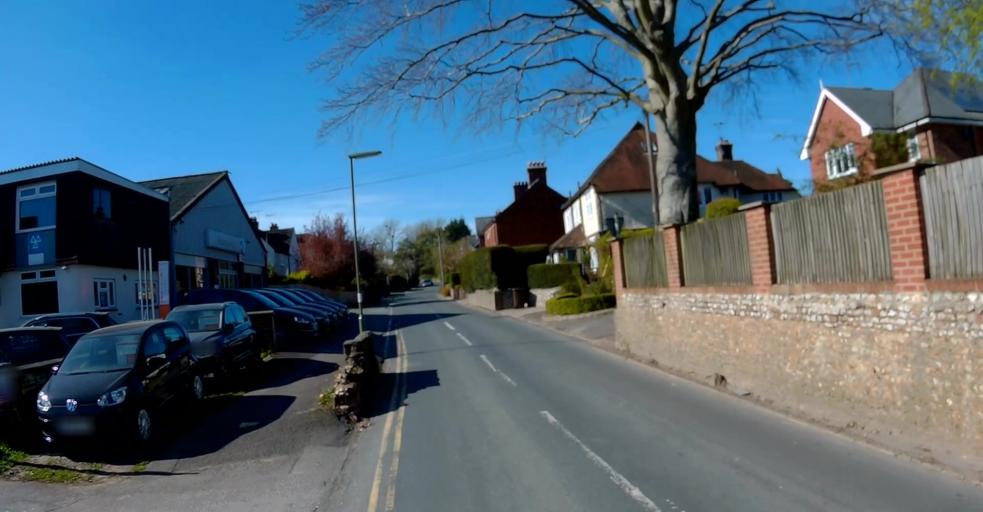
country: GB
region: England
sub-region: Surrey
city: Farnham
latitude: 51.2121
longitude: -0.8079
